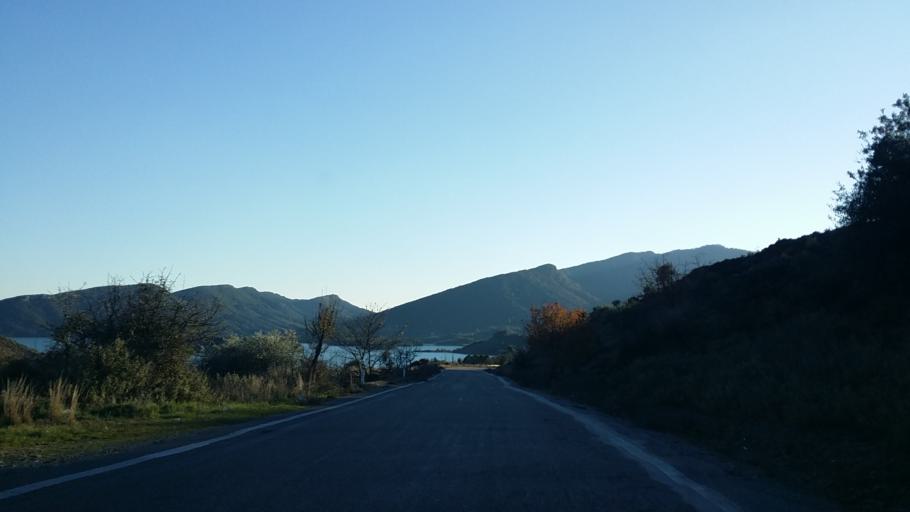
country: GR
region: West Greece
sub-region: Nomos Aitolias kai Akarnanias
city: Sardinia
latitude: 38.8407
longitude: 21.3315
